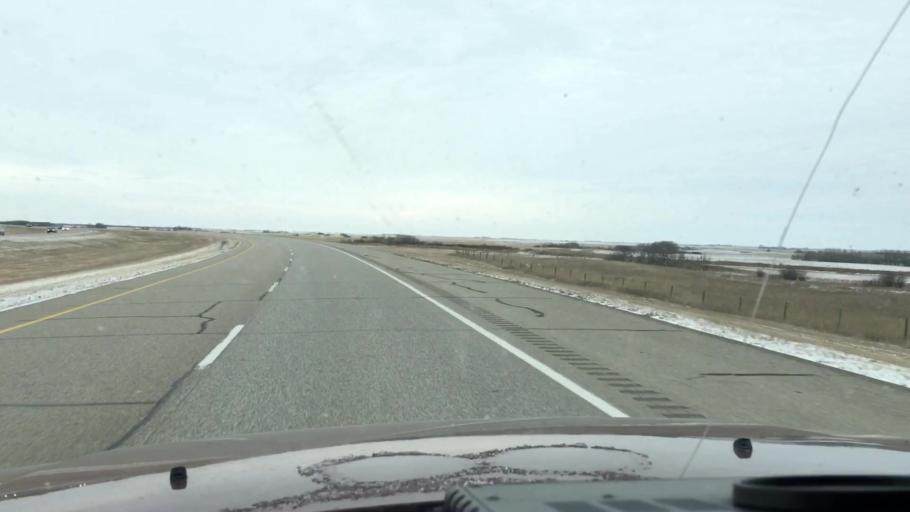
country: CA
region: Saskatchewan
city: Watrous
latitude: 51.3545
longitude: -106.1222
